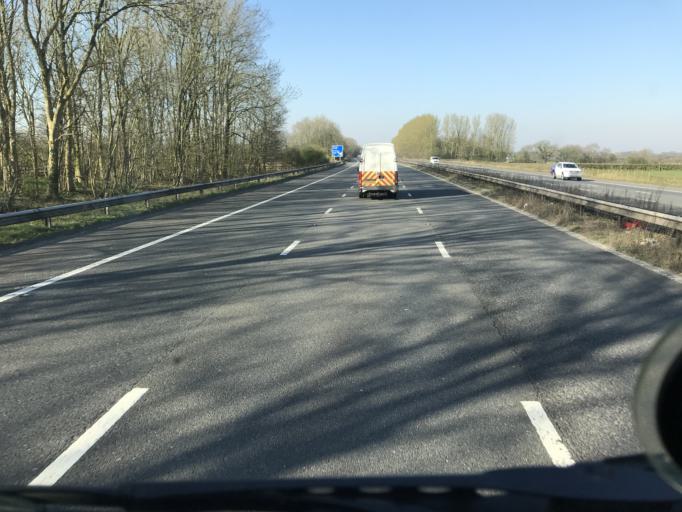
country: GB
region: England
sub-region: Borough of Halton
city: Daresbury
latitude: 53.3315
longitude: -2.6104
